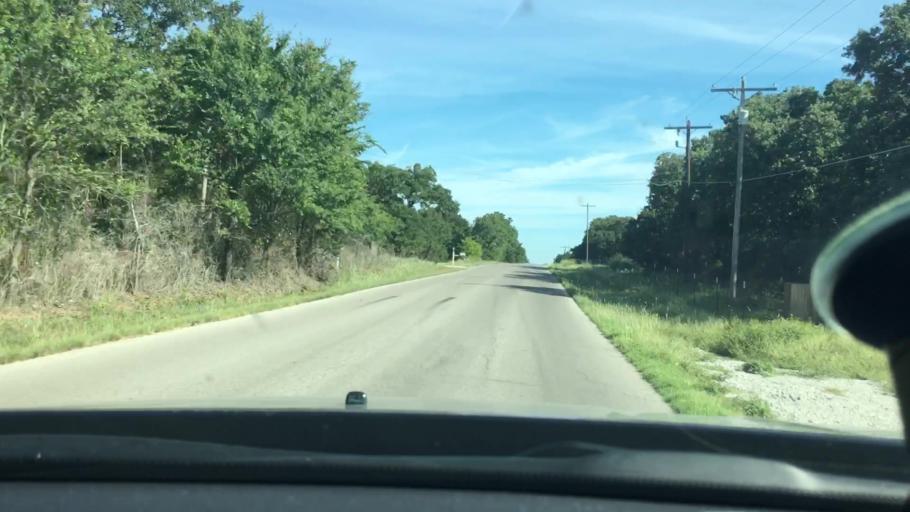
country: US
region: Oklahoma
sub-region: Carter County
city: Lone Grove
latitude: 34.2351
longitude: -97.2474
